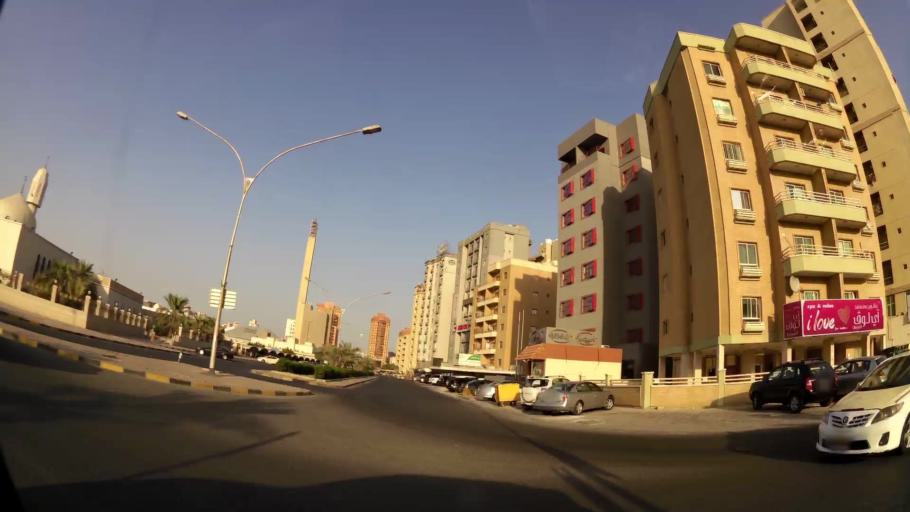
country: KW
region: Muhafazat Hawalli
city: As Salimiyah
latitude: 29.3361
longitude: 48.0801
